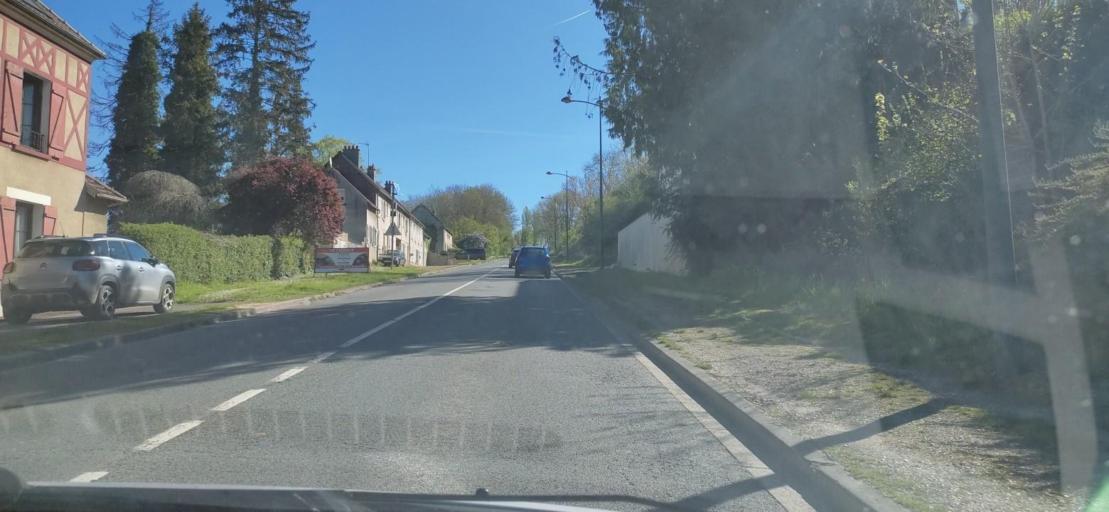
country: FR
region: Picardie
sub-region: Departement de l'Oise
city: Villers-sur-Coudun
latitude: 49.4620
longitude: 2.7646
